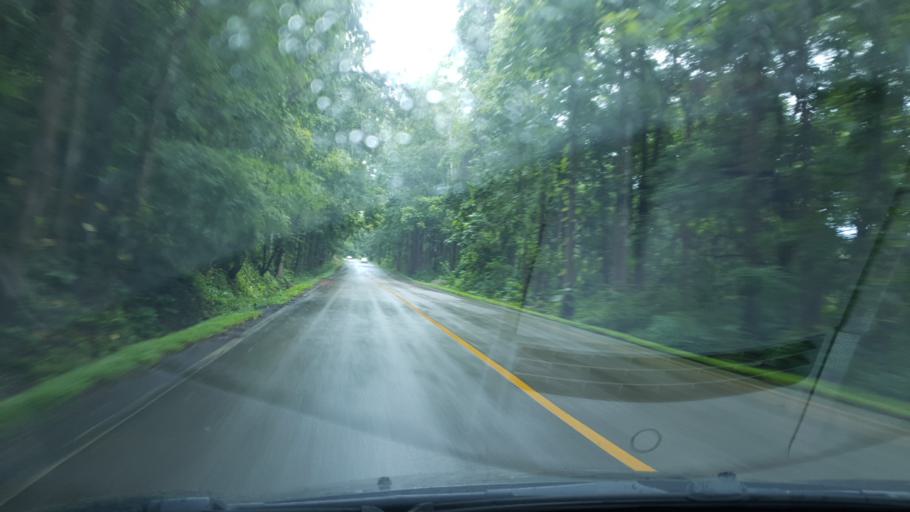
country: TH
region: Mae Hong Son
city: Pa Pae
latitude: 18.2560
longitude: 97.9418
